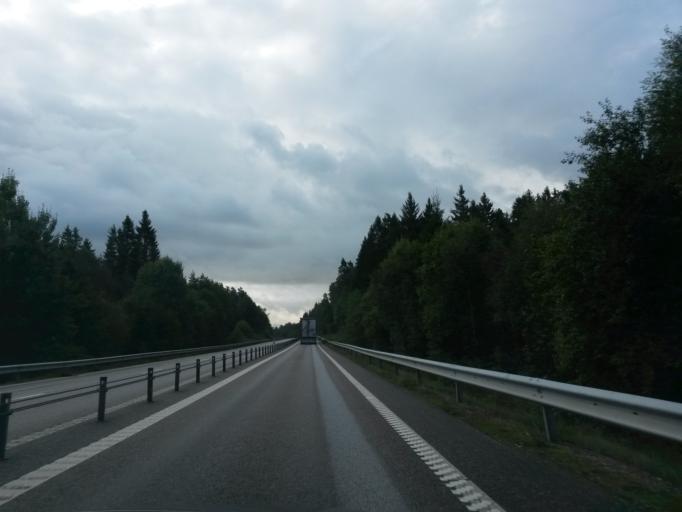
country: SE
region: Vaestra Goetaland
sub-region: Boras Kommun
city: Dalsjofors
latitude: 57.6226
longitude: 13.1019
